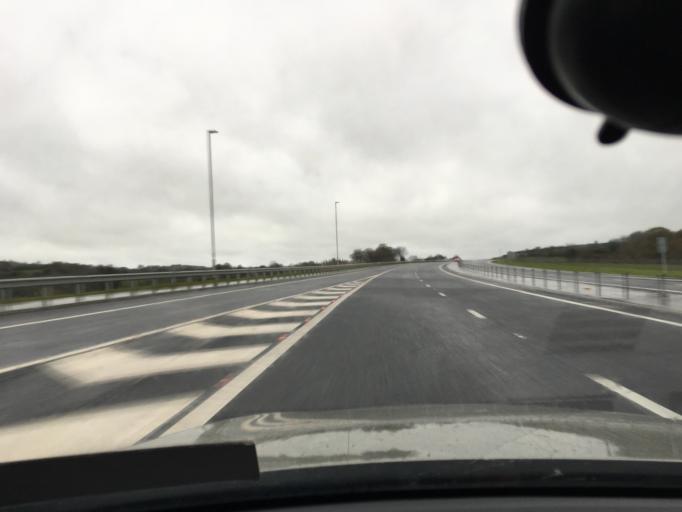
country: GB
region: Northern Ireland
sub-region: Larne District
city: Larne
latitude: 54.8150
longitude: -5.8985
